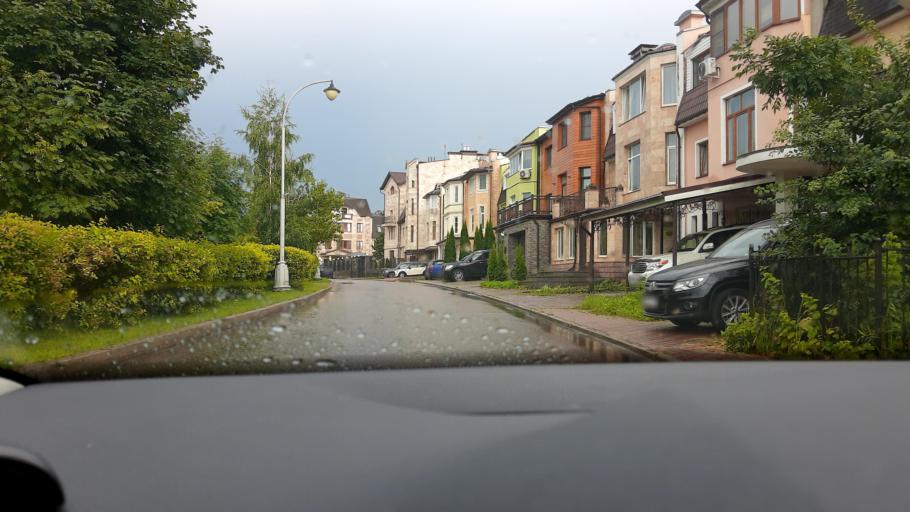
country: RU
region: Moskovskaya
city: Novopodrezkovo
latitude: 55.8789
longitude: 37.3614
